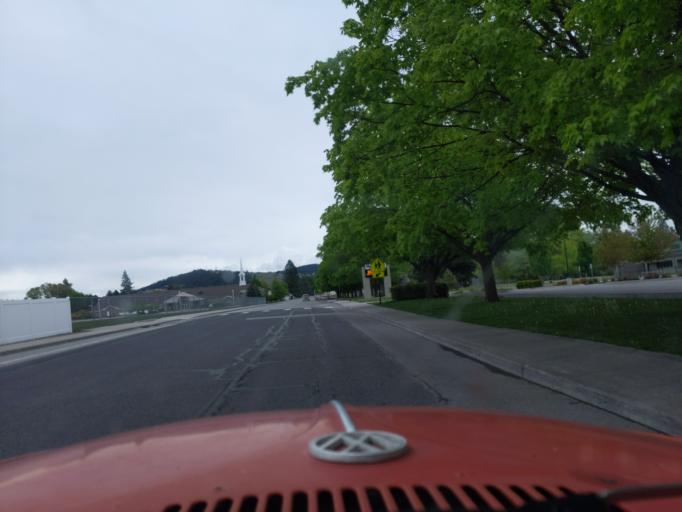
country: US
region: Washington
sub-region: Spokane County
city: Spokane
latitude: 47.5967
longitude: -117.3733
